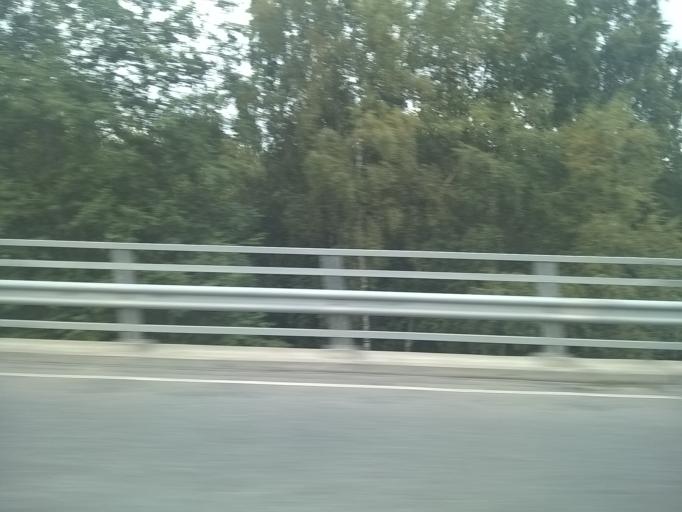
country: FI
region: Pirkanmaa
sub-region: Tampere
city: Tampere
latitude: 61.4723
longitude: 23.8378
